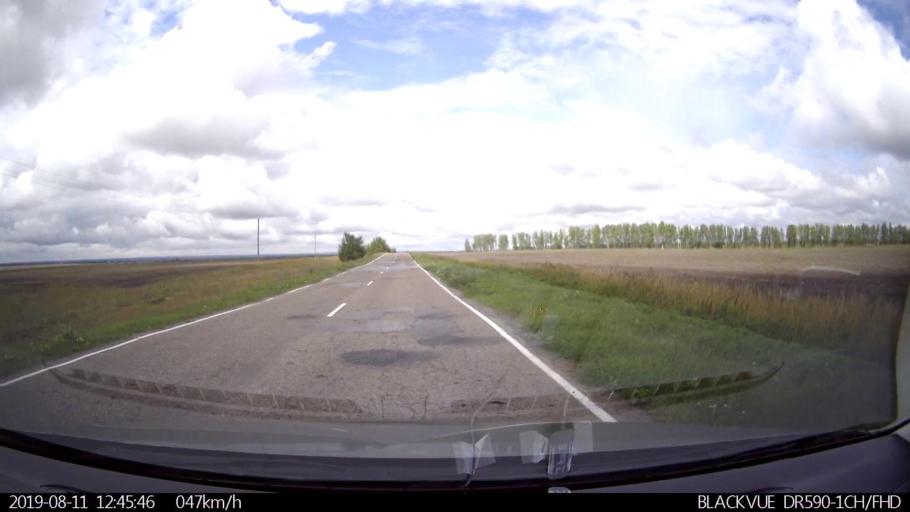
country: RU
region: Ulyanovsk
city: Ignatovka
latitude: 53.8610
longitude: 47.7250
